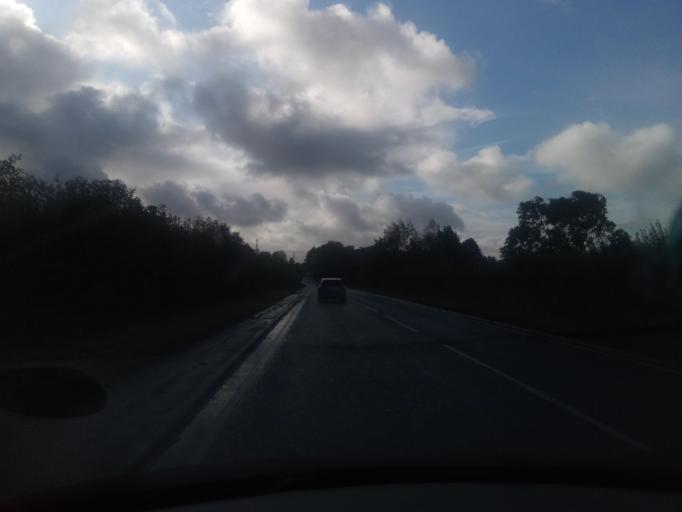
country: GB
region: England
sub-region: Cumbria
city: Carlisle
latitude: 54.9474
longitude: -2.9433
